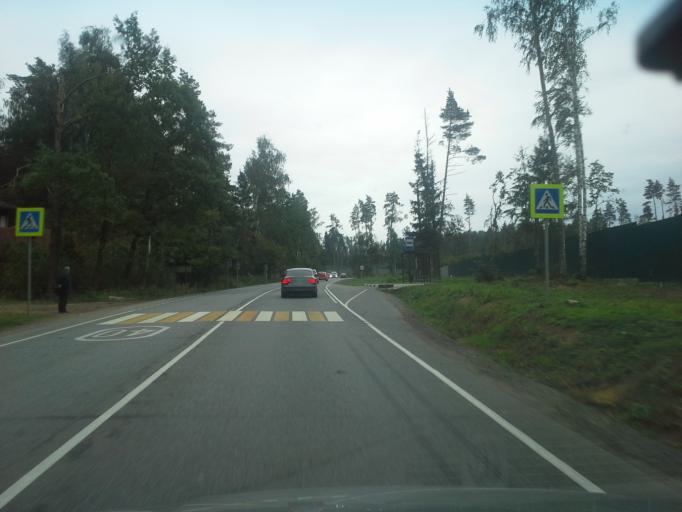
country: RU
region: Moskovskaya
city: Zhavoronki
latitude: 55.7054
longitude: 37.0989
